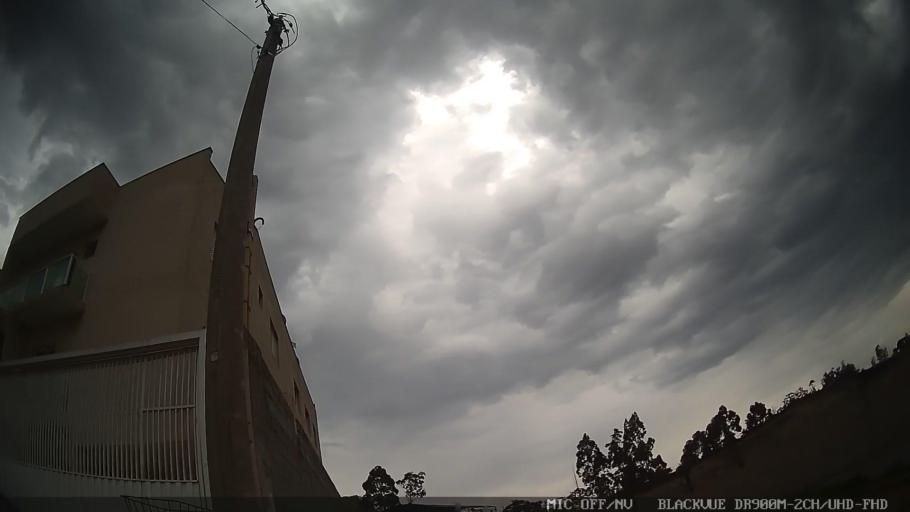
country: BR
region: Sao Paulo
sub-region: Itatiba
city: Itatiba
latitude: -23.0053
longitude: -46.8629
